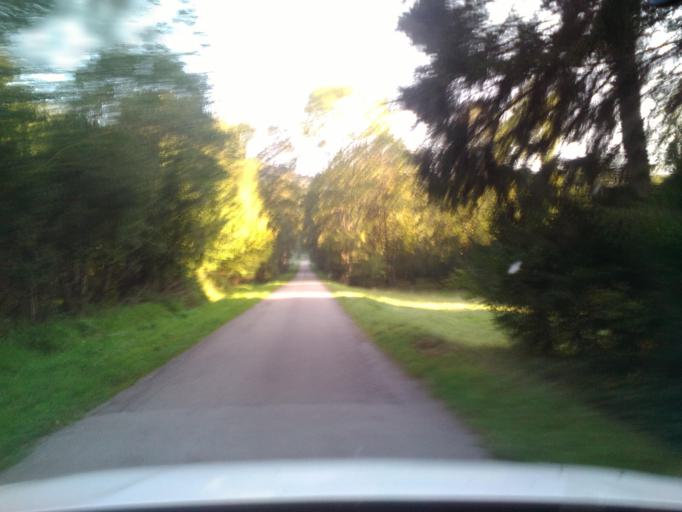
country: FR
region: Lorraine
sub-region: Departement des Vosges
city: Ban-de-Laveline
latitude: 48.3328
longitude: 7.0878
